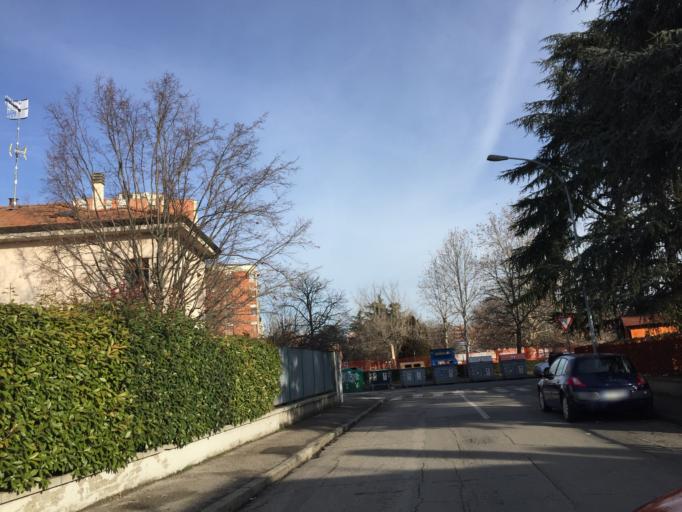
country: IT
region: Emilia-Romagna
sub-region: Provincia di Bologna
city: Casalecchio di Reno
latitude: 44.4996
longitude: 11.2938
